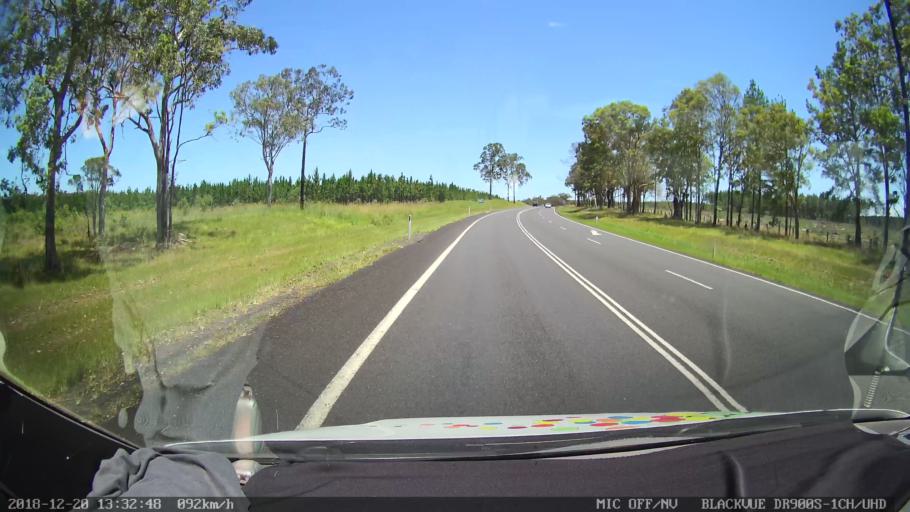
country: AU
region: New South Wales
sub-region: Clarence Valley
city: Gordon
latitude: -29.2366
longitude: 152.9889
